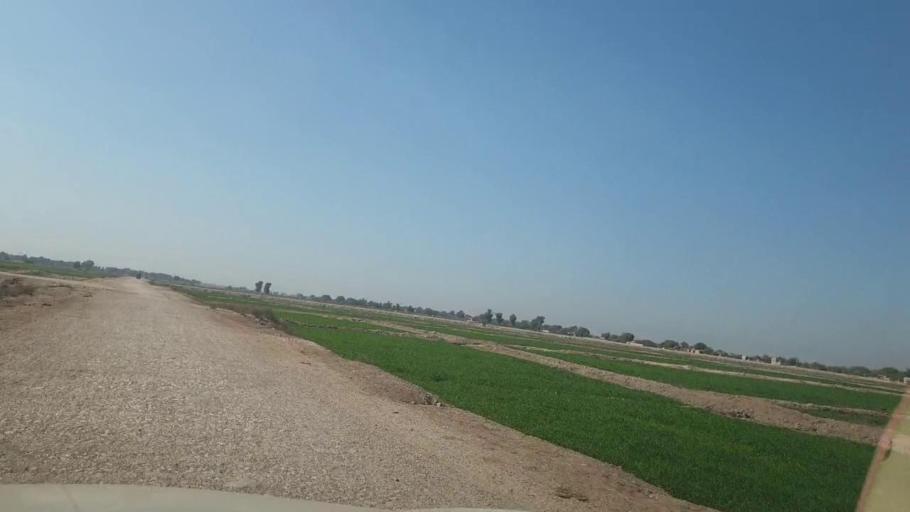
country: PK
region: Sindh
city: Bhan
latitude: 26.5647
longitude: 67.6940
